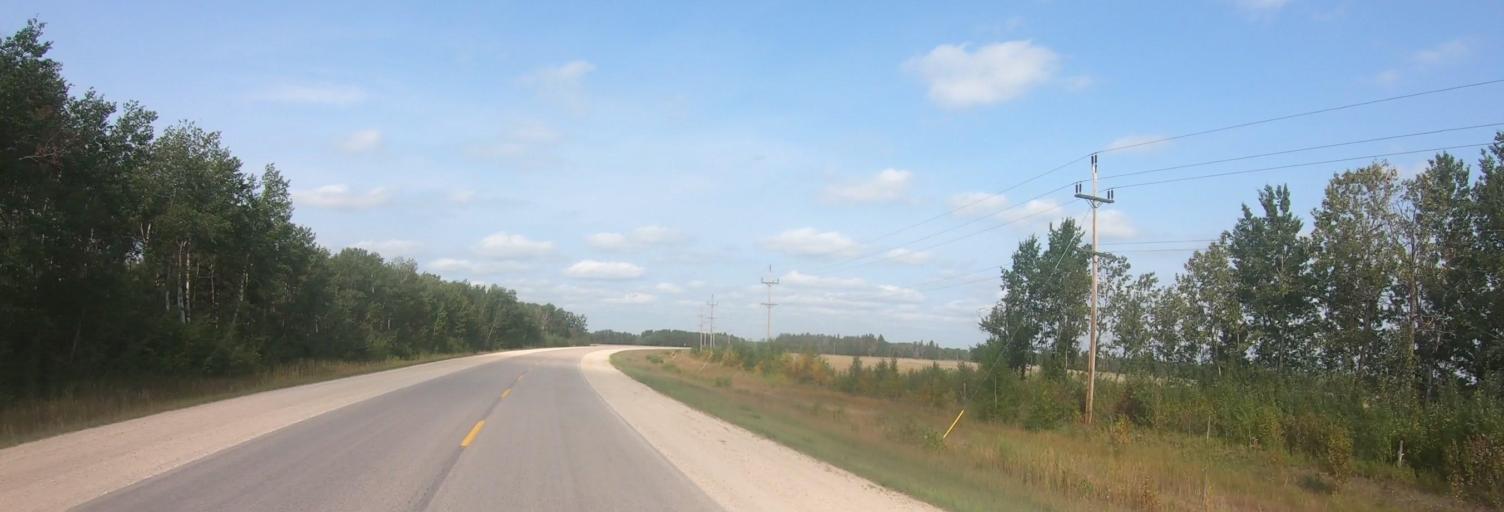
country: CA
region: Manitoba
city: La Broquerie
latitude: 49.1781
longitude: -96.2278
